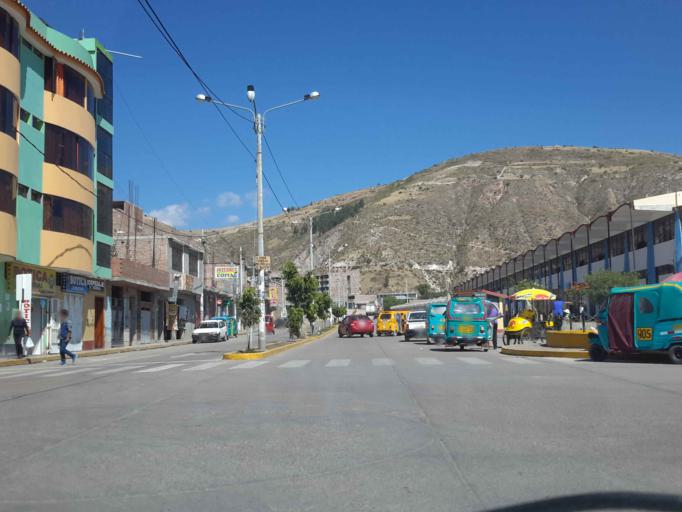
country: PE
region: Ayacucho
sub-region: Provincia de Huamanga
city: Ayacucho
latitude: -13.1345
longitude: -74.2296
